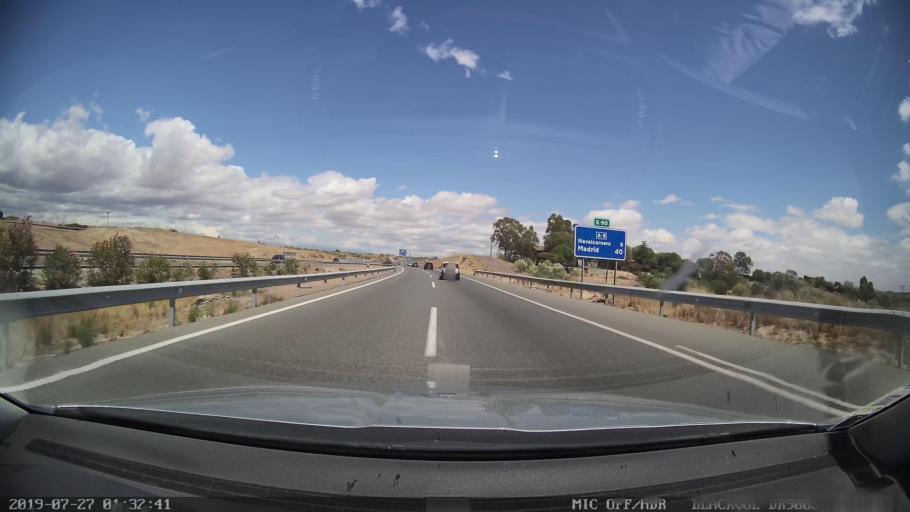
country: ES
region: Castille-La Mancha
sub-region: Province of Toledo
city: Valmojado
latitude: 40.2229
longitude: -4.0743
